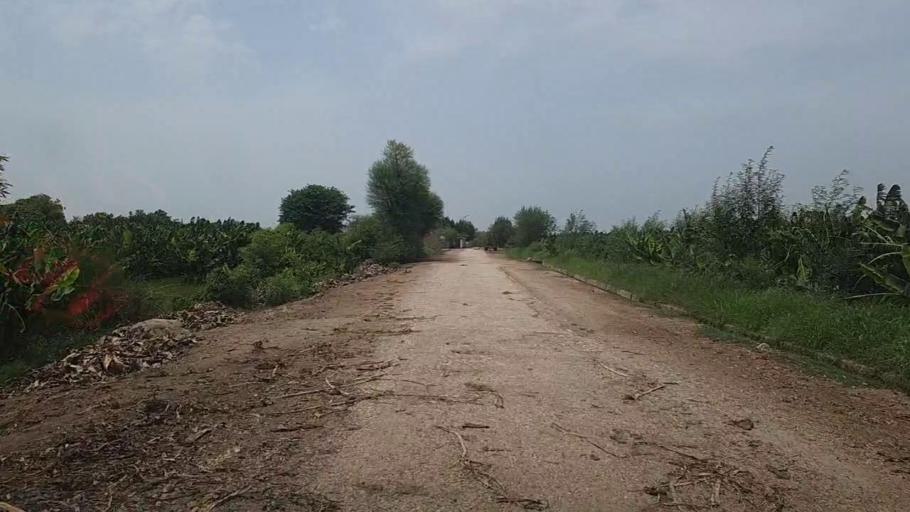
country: PK
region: Sindh
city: Karaundi
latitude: 26.9171
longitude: 68.3343
